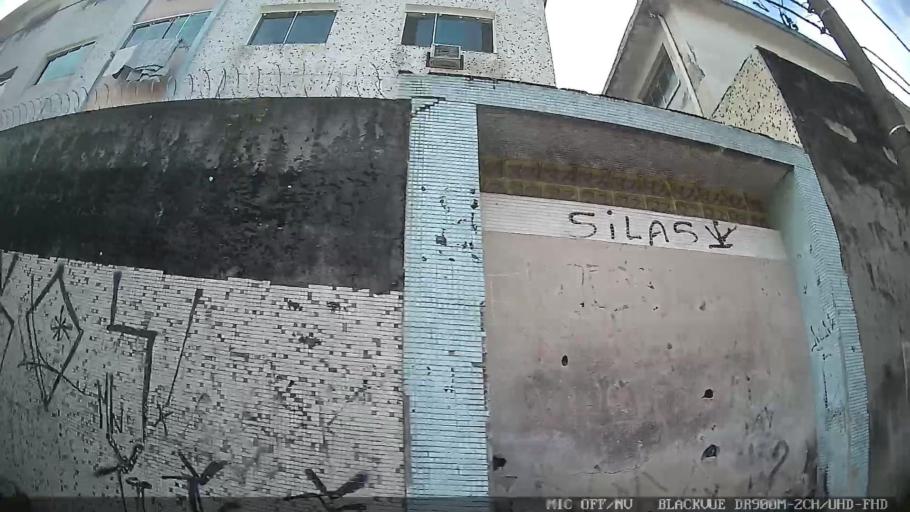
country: BR
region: Sao Paulo
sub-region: Santos
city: Santos
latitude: -23.9443
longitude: -46.3003
